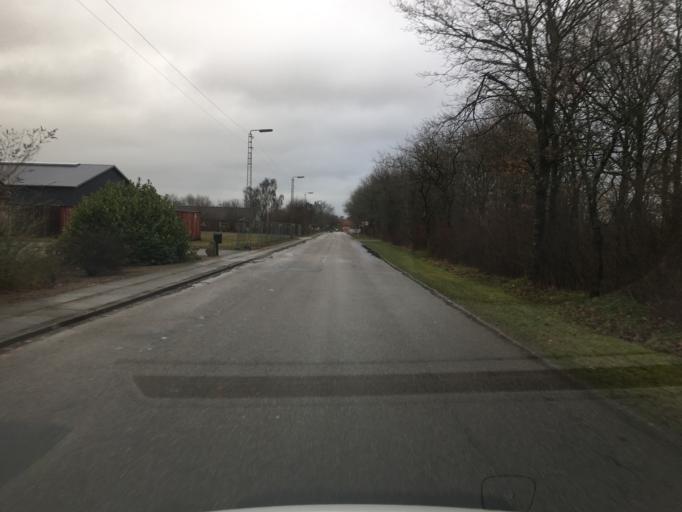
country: DK
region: South Denmark
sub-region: Aabenraa Kommune
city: Tinglev
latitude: 54.9283
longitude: 9.2358
